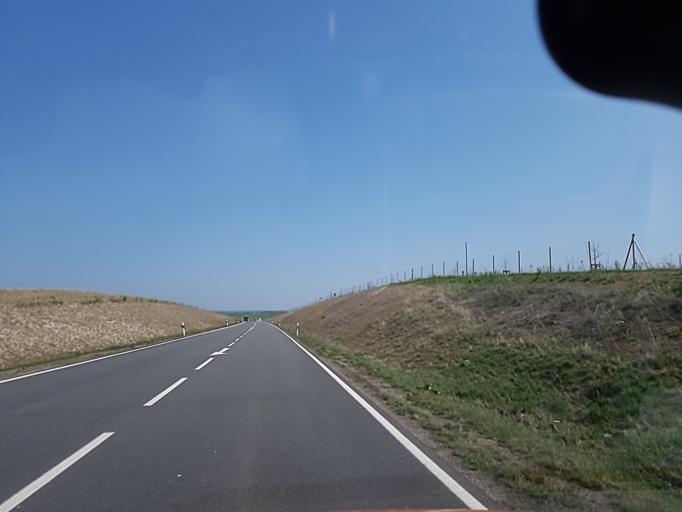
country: DE
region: Saxony
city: Mutzschen
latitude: 51.2603
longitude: 12.9085
